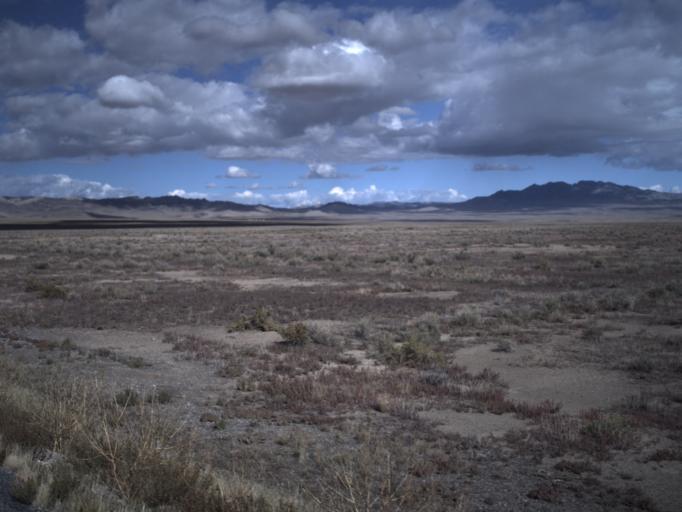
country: US
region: Utah
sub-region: Beaver County
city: Milford
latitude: 38.5409
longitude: -113.7050
